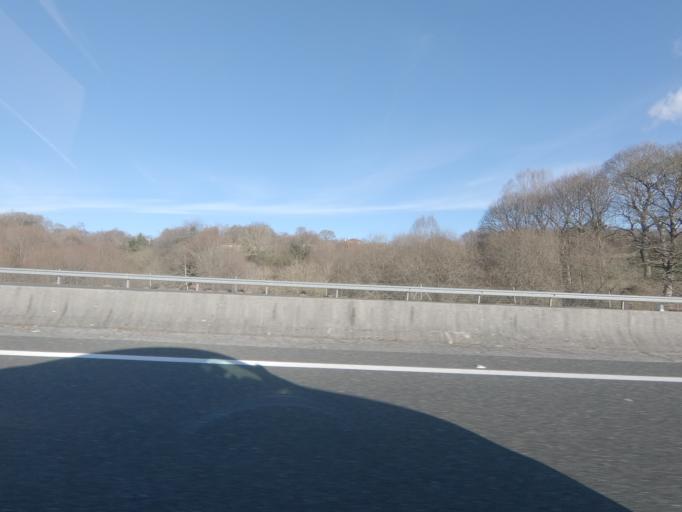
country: ES
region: Galicia
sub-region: Provincia de Pontevedra
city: Lalin
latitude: 42.6444
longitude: -8.1326
